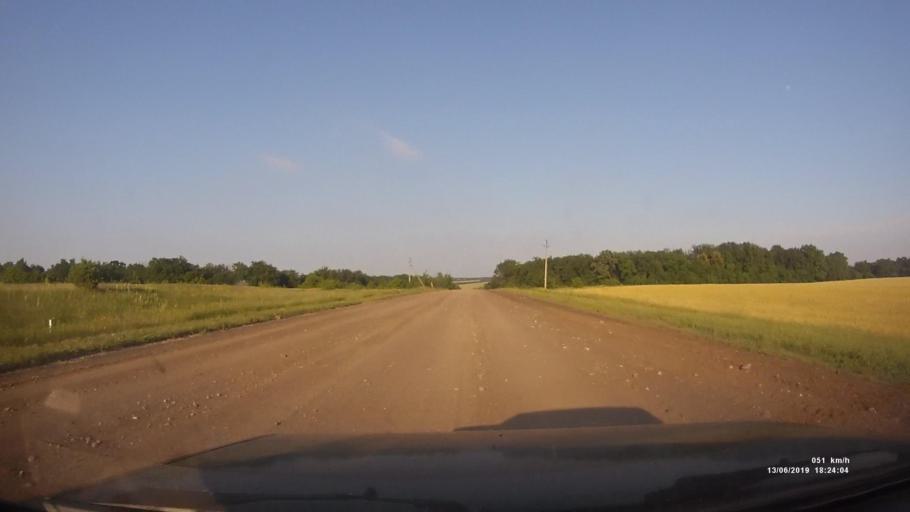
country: RU
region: Rostov
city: Kazanskaya
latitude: 49.8522
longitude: 41.2858
